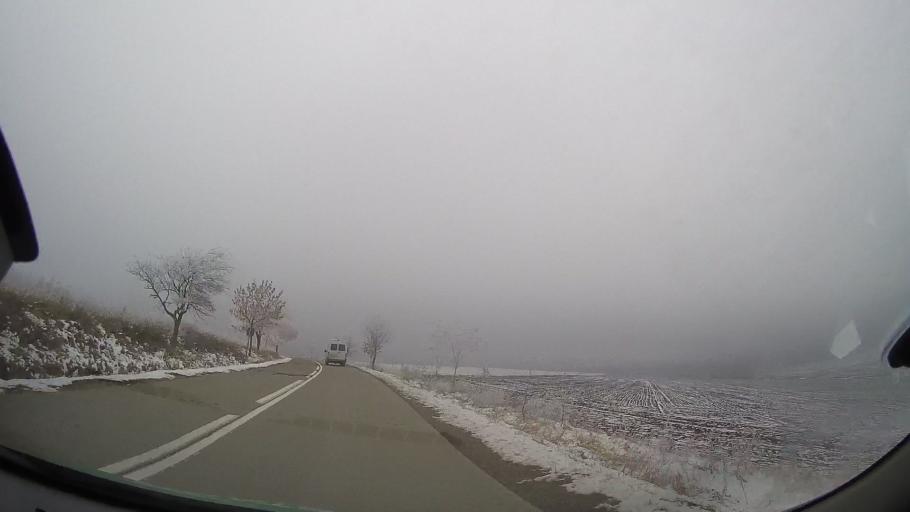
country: RO
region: Vaslui
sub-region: Comuna Ivesti
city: Ivesti
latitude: 46.1963
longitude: 27.5971
